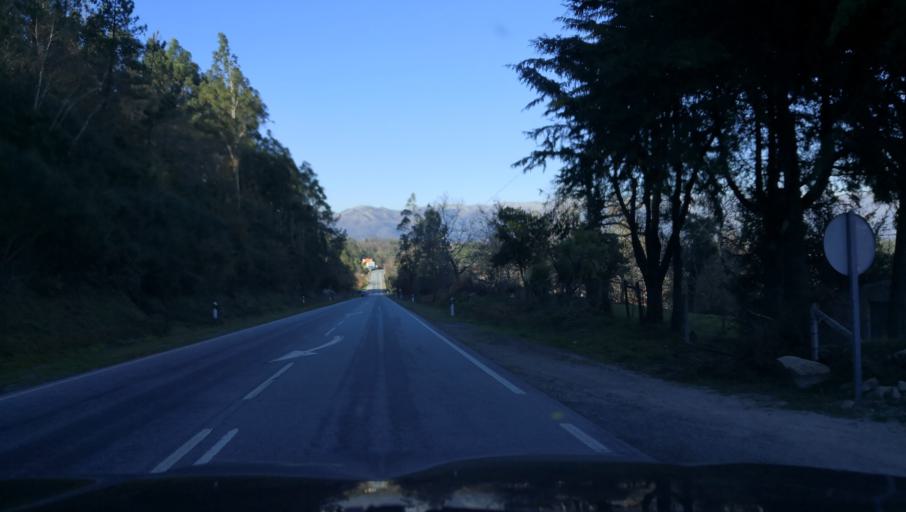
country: PT
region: Viseu
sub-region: Vouzela
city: Vouzela
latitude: 40.7007
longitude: -8.1402
